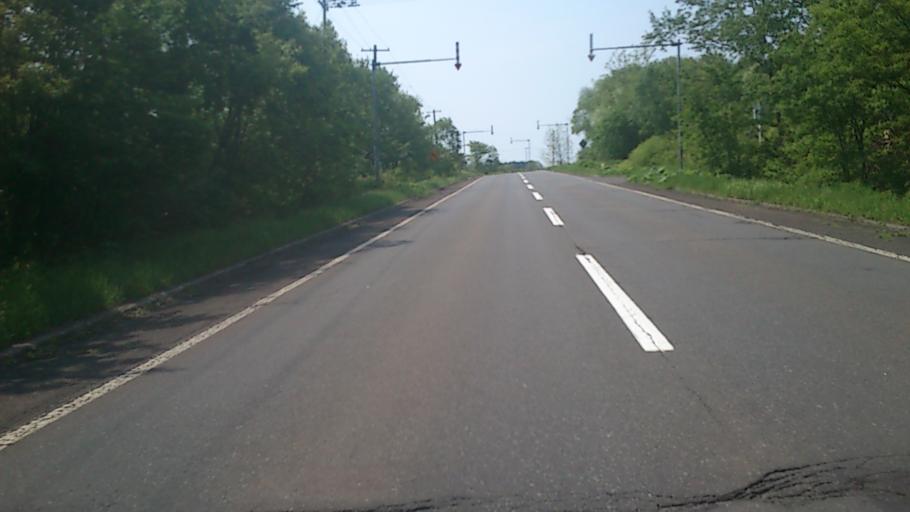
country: JP
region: Hokkaido
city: Shibetsu
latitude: 43.4558
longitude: 144.6925
